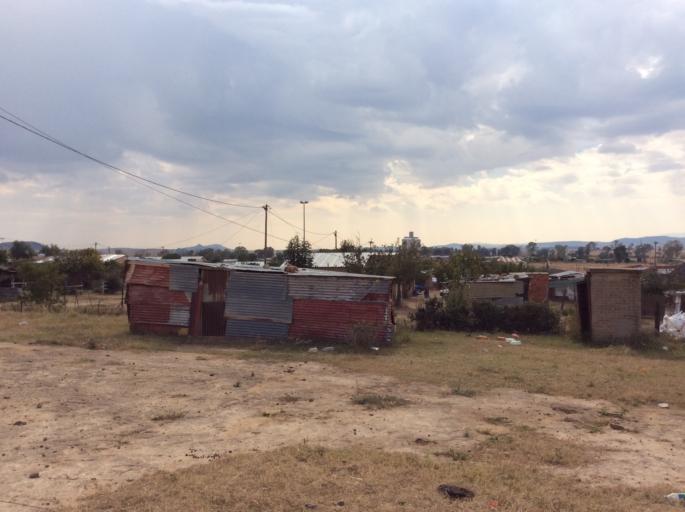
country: ZA
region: Orange Free State
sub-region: Xhariep District Municipality
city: Dewetsdorp
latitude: -29.5803
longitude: 26.6841
